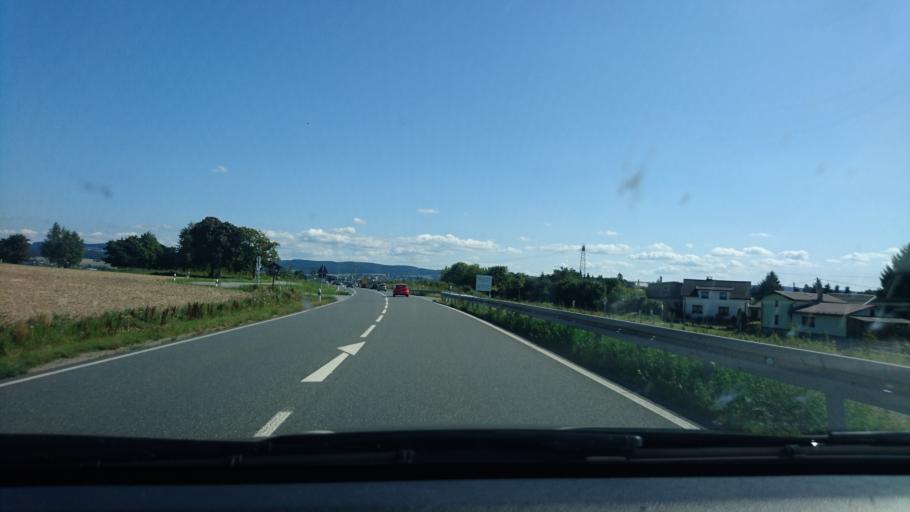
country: DE
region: Saxony
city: Auerbach
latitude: 50.5273
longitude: 12.3772
